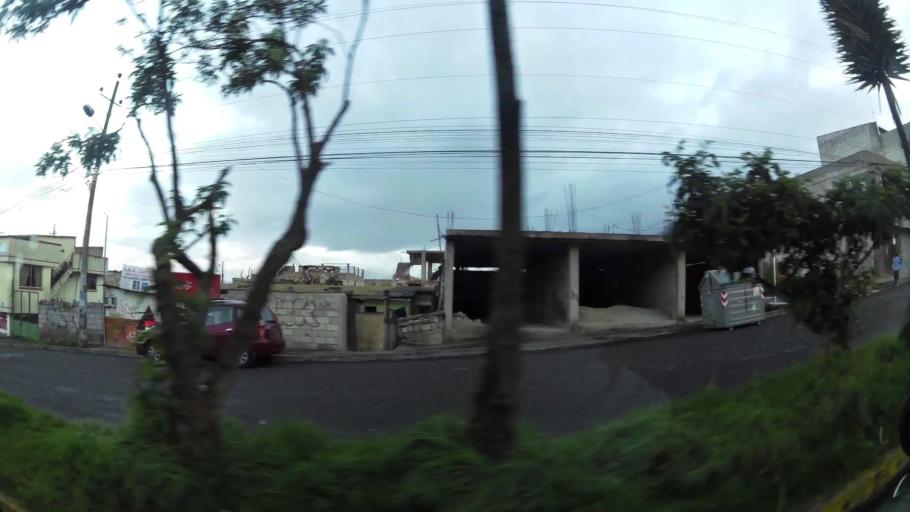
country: EC
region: Pichincha
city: Quito
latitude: -0.0910
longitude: -78.5207
